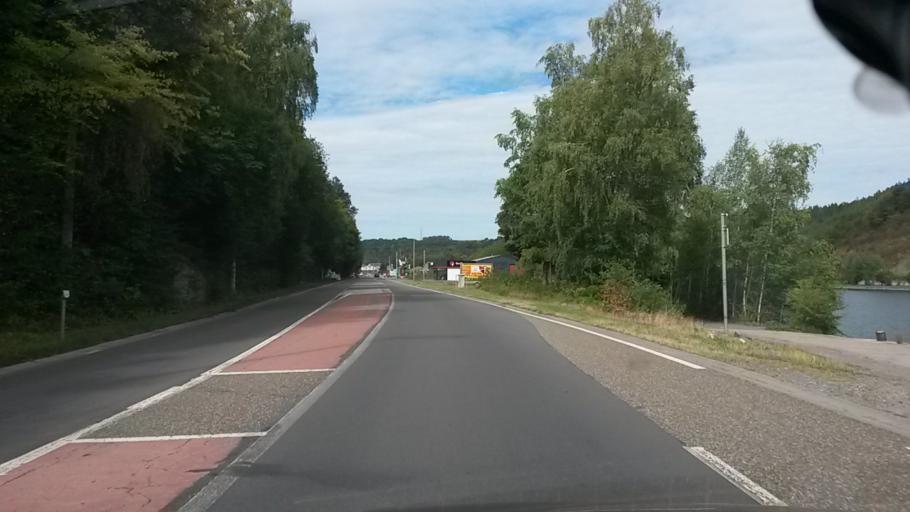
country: BE
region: Wallonia
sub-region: Province de Namur
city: Andenne
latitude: 50.4935
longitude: 5.0622
